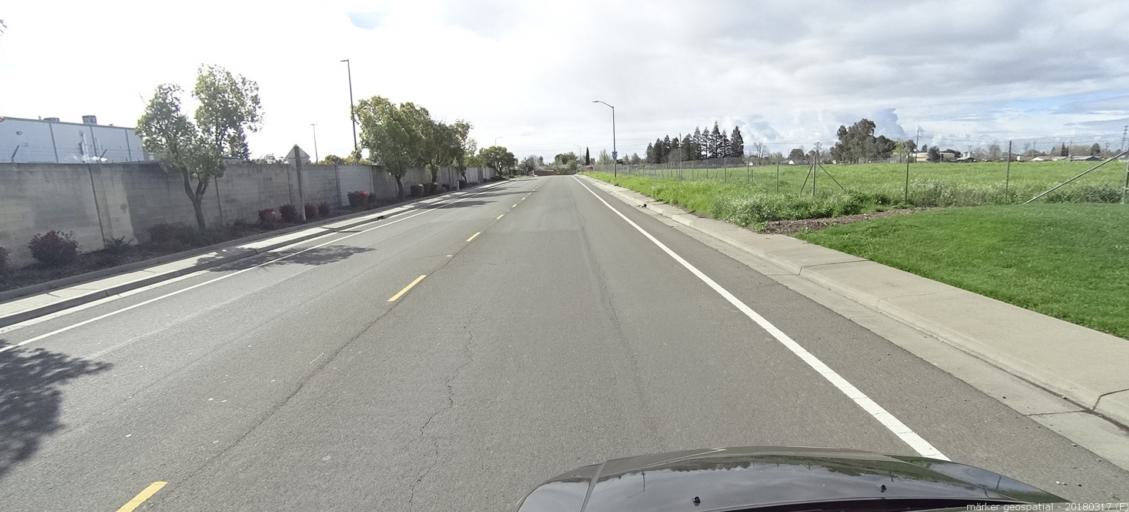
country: US
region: California
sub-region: Sacramento County
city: Florin
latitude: 38.4764
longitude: -121.3968
